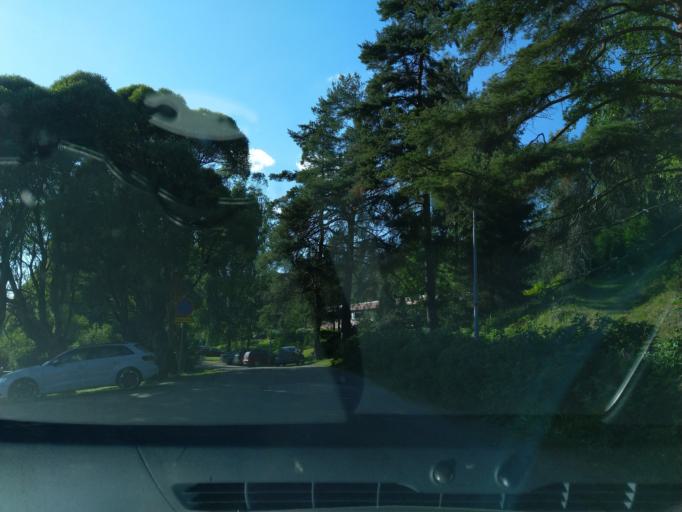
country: FI
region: Pirkanmaa
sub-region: Ylae-Pirkanmaa
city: Virrat
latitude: 62.2393
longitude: 23.7532
